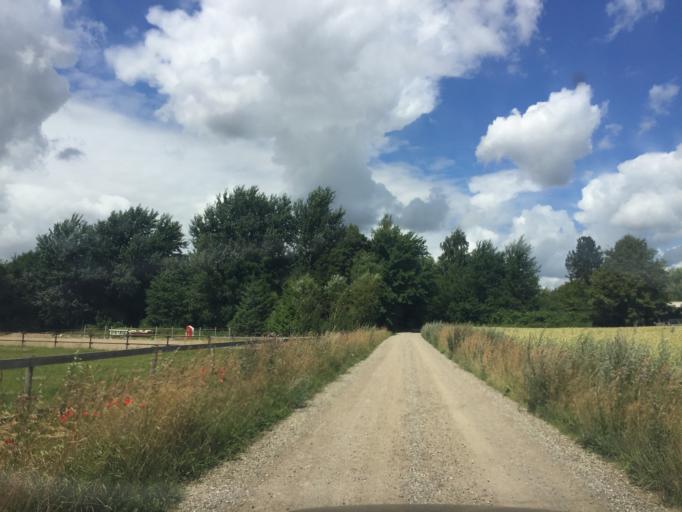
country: DK
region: Capital Region
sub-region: Egedal Kommune
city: Smorumnedre
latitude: 55.7062
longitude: 12.2671
